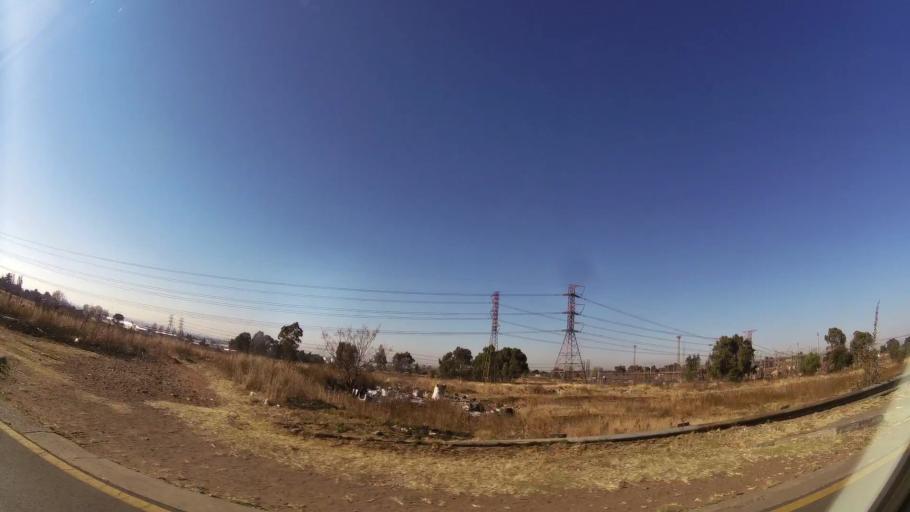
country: ZA
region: Gauteng
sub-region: Ekurhuleni Metropolitan Municipality
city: Germiston
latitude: -26.3043
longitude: 28.1152
